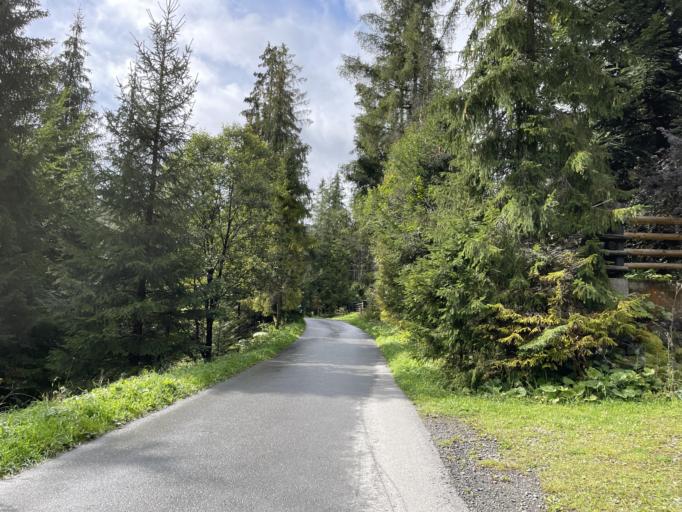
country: PL
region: Silesian Voivodeship
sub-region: Powiat zywiecki
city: Ujsoly
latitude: 49.4752
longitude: 19.1275
